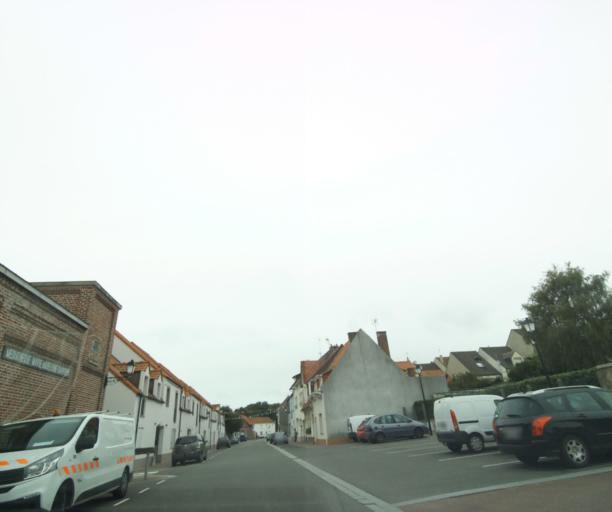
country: FR
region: Nord-Pas-de-Calais
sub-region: Departement du Pas-de-Calais
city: Etaples
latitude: 50.5181
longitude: 1.6322
